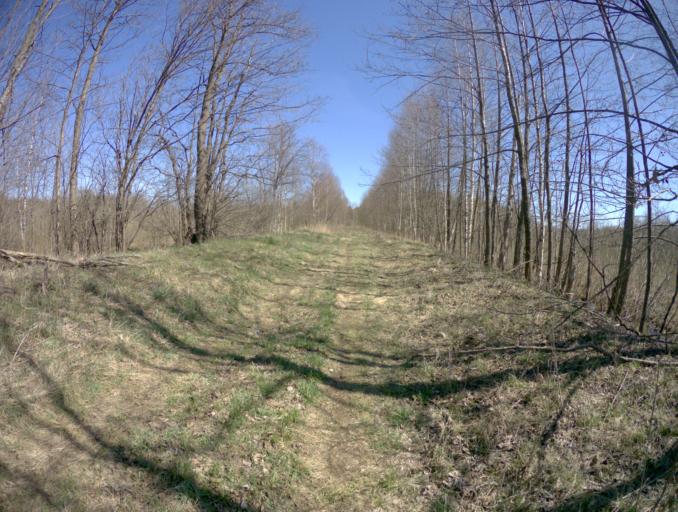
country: RU
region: Vladimir
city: Ivanishchi
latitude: 55.8626
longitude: 40.4242
